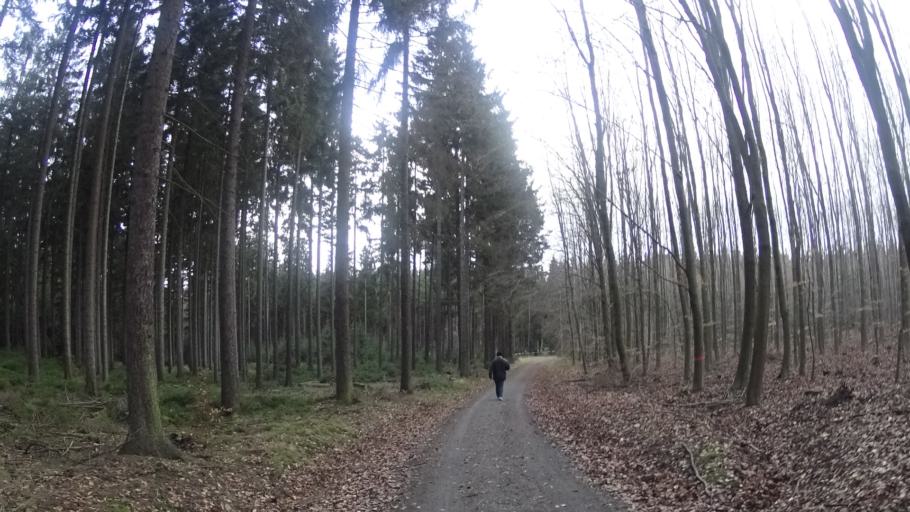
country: DE
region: Thuringia
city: Langenwolschendorf
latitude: 50.6164
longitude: 11.9844
